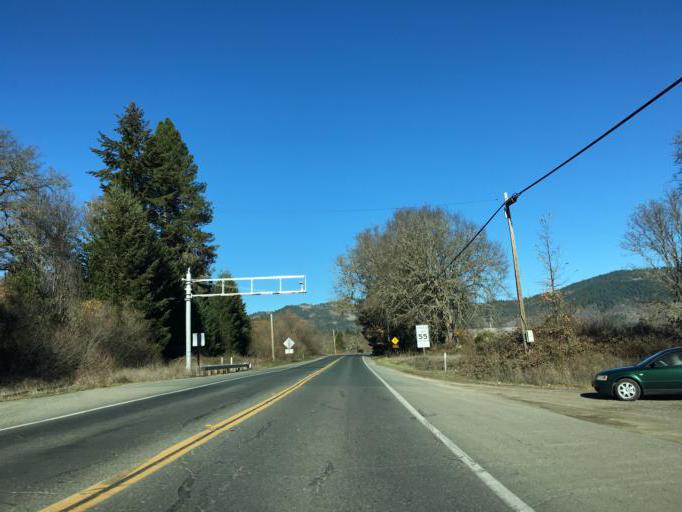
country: US
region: California
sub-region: Mendocino County
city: Brooktrails
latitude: 39.4404
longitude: -123.3556
